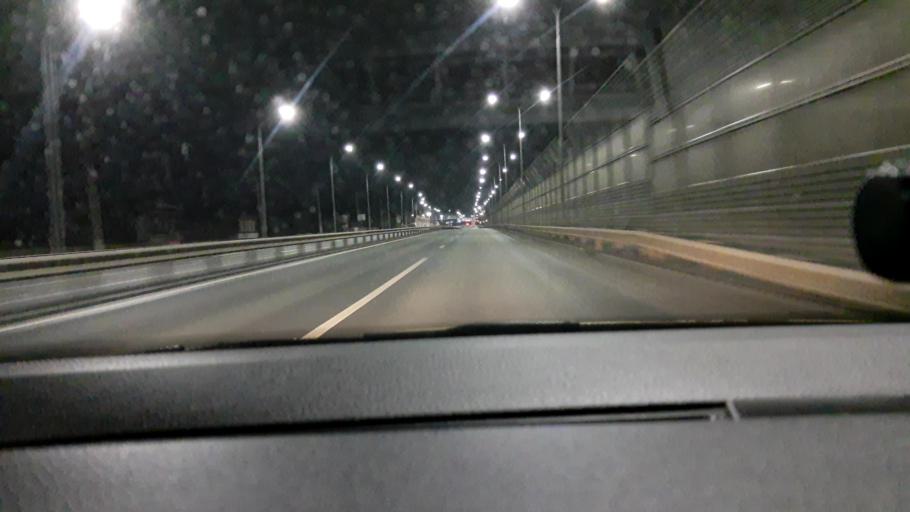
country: RU
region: Vladimir
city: Sobinka
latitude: 56.0319
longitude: 40.0160
